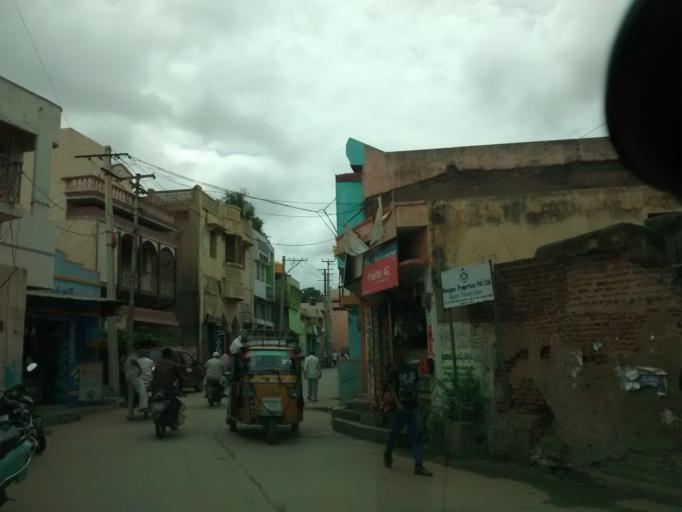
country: IN
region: Andhra Pradesh
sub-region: Anantapur
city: Hindupur
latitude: 13.8249
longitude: 77.4896
